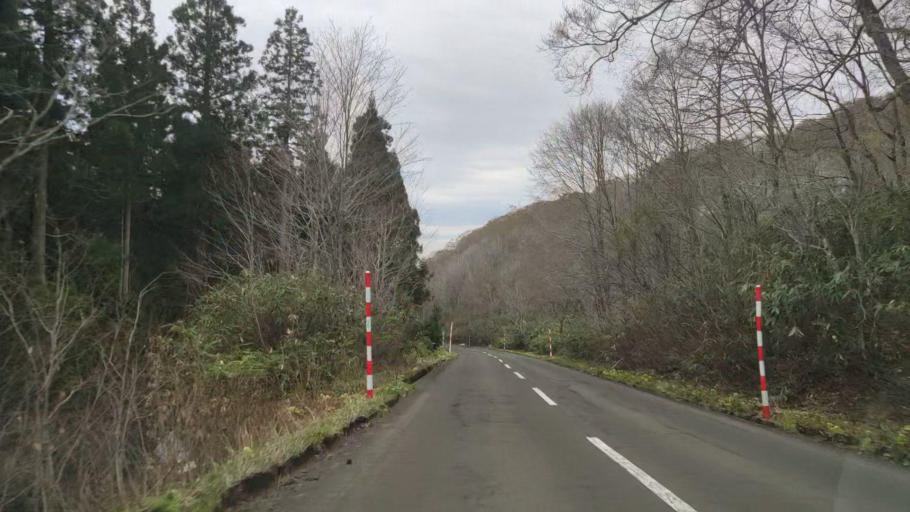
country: JP
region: Akita
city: Hanawa
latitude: 40.4138
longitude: 140.8188
